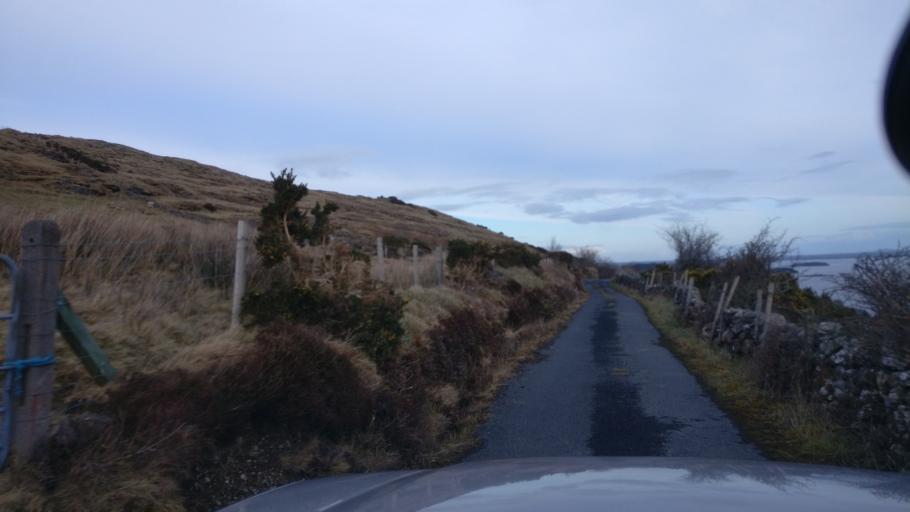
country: IE
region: Connaught
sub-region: County Galway
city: Oughterard
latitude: 53.5212
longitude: -9.4102
